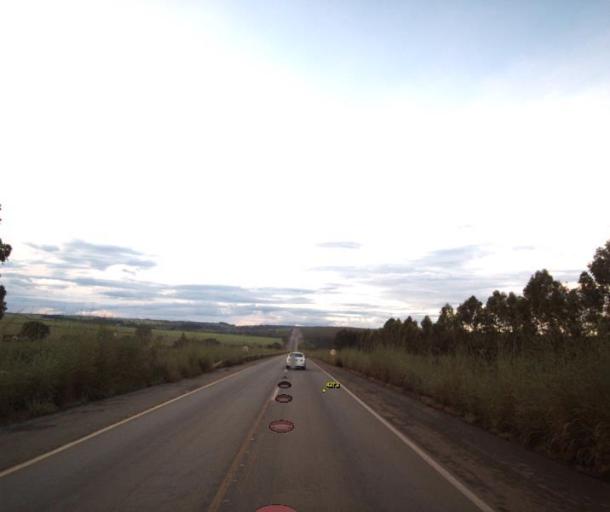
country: BR
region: Goias
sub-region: Anapolis
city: Anapolis
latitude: -16.2241
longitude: -49.0120
